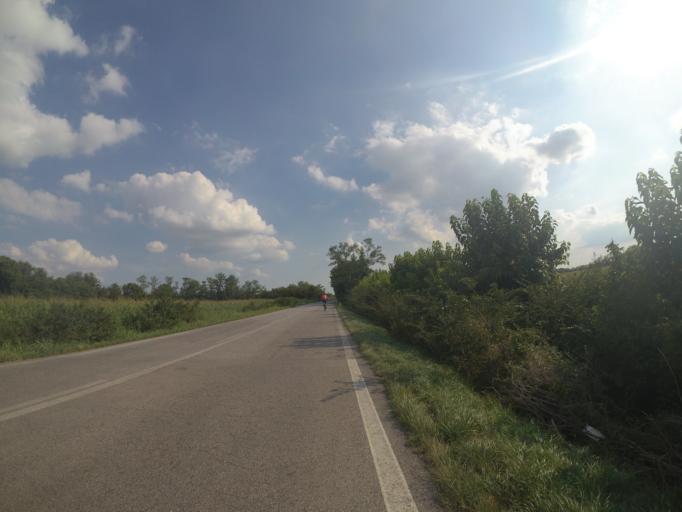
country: IT
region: Friuli Venezia Giulia
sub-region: Provincia di Udine
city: San Vito di Fagagna
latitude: 46.0794
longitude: 13.0860
